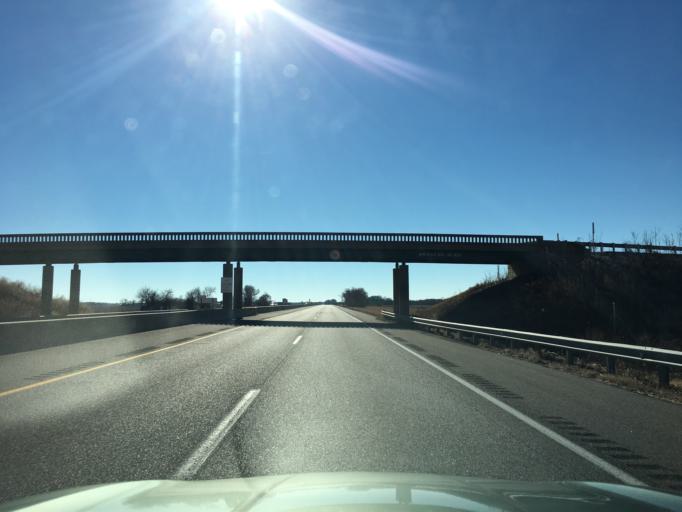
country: US
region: Kansas
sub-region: Sumner County
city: Mulvane
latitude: 37.4653
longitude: -97.3227
